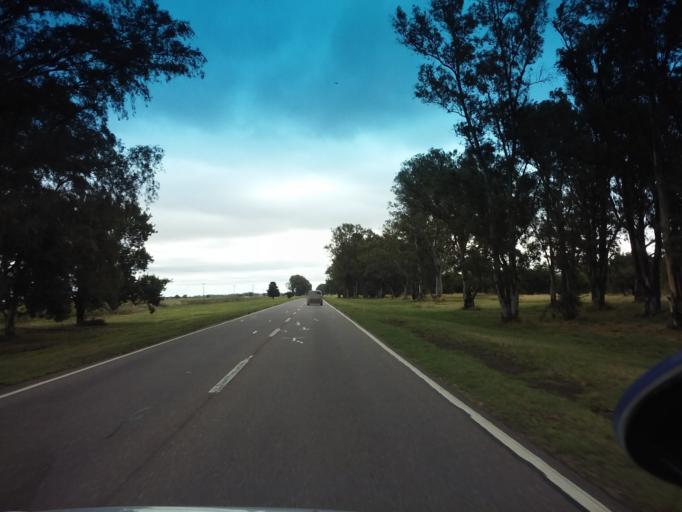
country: AR
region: La Pampa
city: Santa Rosa
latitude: -36.5737
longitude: -64.1547
